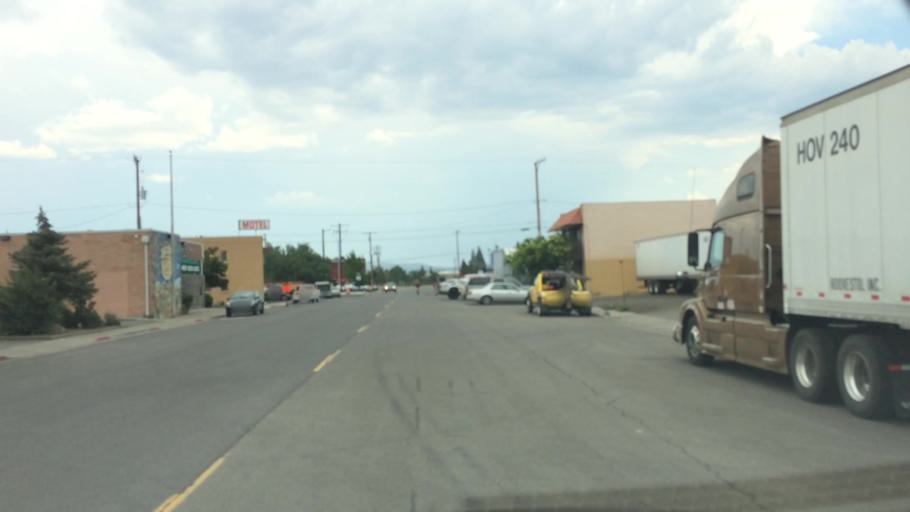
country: US
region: Nevada
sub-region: Washoe County
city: Reno
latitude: 39.5337
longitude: -119.8007
